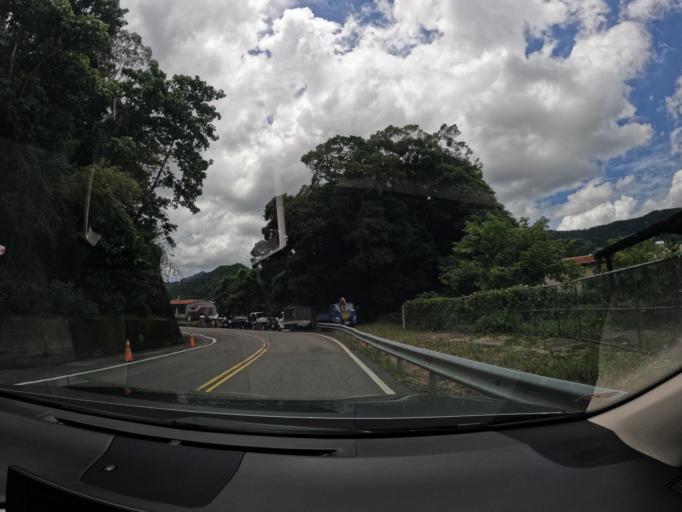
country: TW
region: Taiwan
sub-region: Miaoli
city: Miaoli
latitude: 24.5949
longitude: 121.0007
